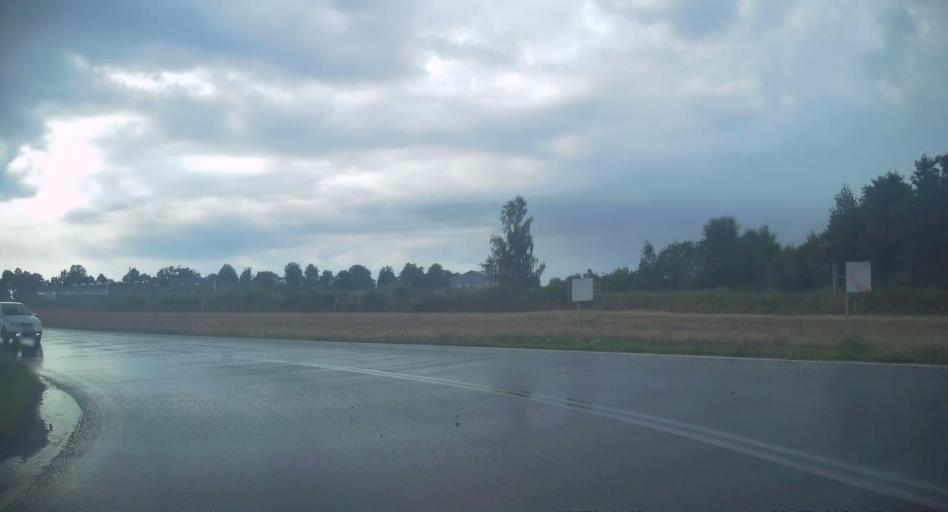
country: PL
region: Lodz Voivodeship
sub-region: Powiat brzezinski
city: Rogow
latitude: 51.8069
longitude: 19.8764
